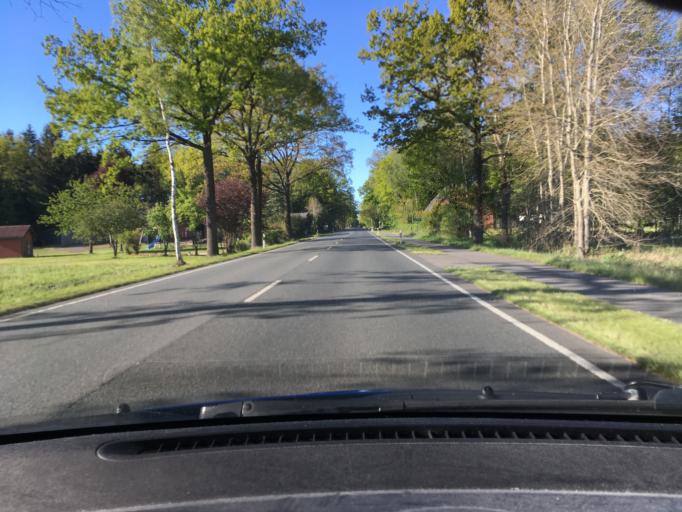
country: DE
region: Lower Saxony
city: Soltau
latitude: 53.0376
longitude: 9.8542
